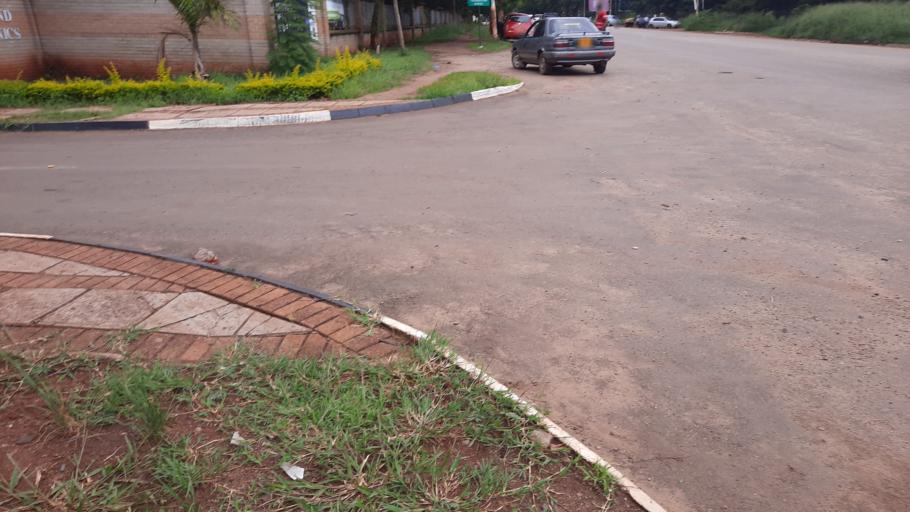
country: ZW
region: Harare
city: Harare
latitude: -17.8202
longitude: 31.0294
